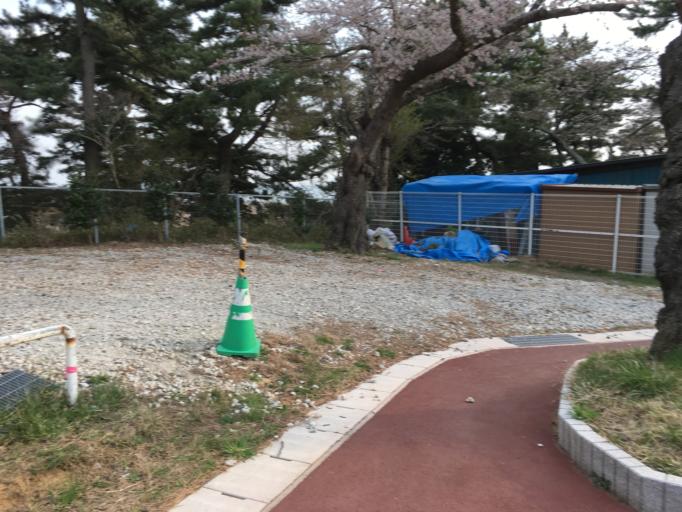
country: JP
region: Miyagi
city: Ishinomaki
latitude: 38.4225
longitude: 141.3061
